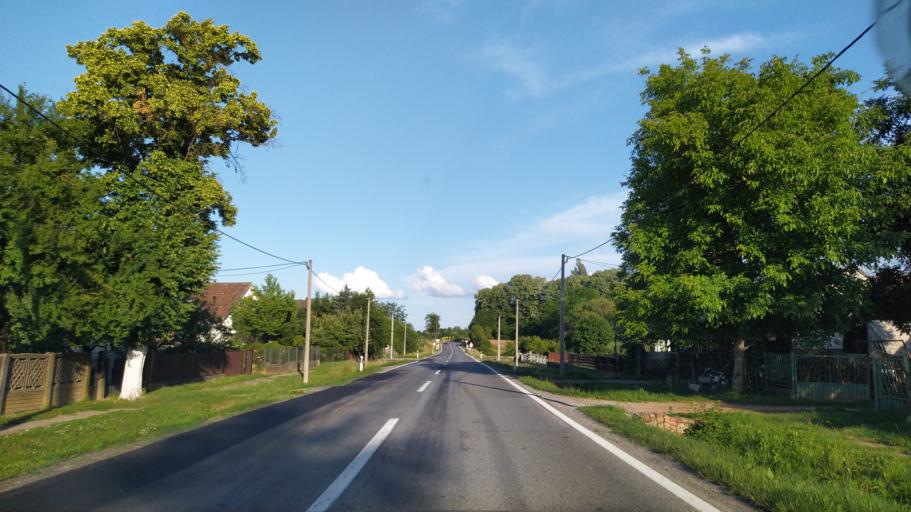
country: HR
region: Virovitick-Podravska
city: Slatina
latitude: 45.6773
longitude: 17.7490
